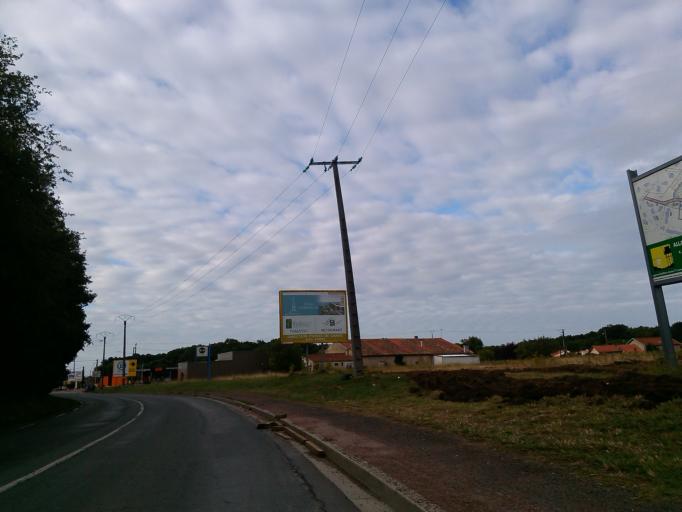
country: FR
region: Poitou-Charentes
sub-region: Departement de la Charente-Maritime
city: Royan
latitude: 45.6502
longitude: -1.0245
